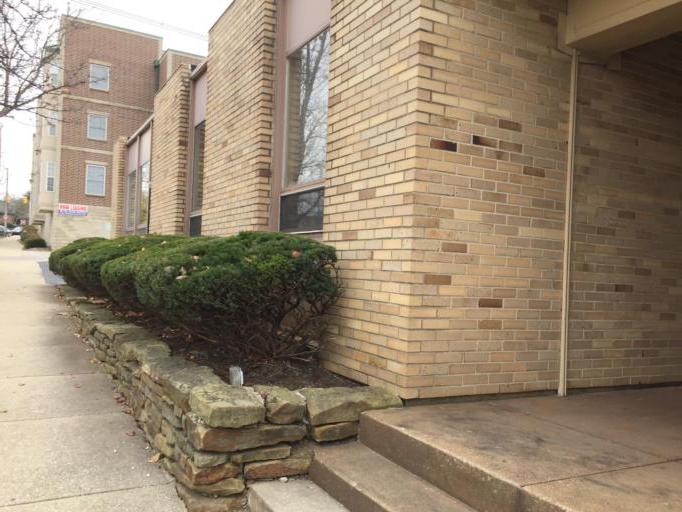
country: US
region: Indiana
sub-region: Monroe County
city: Bloomington
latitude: 39.1645
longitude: -86.5296
